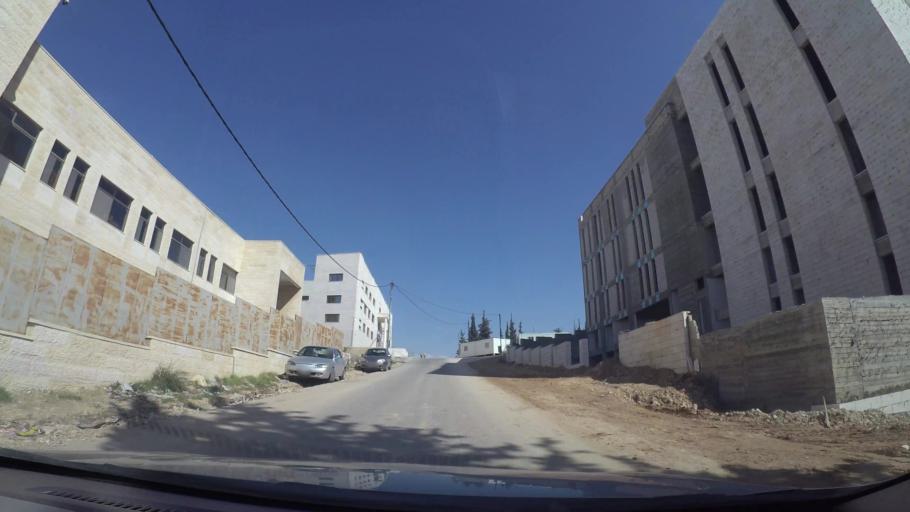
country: JO
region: Amman
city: Al Bunayyat ash Shamaliyah
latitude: 31.9141
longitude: 35.9048
